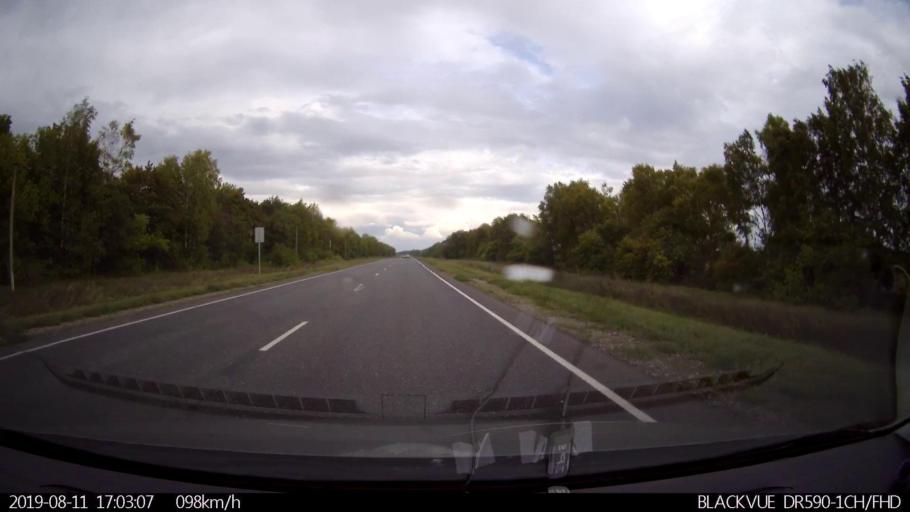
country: RU
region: Ulyanovsk
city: Mayna
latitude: 54.3040
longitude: 47.7316
